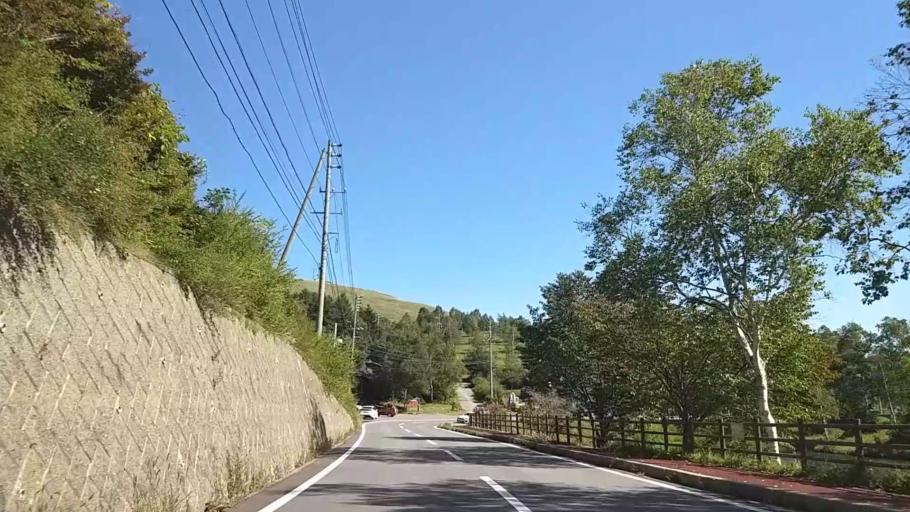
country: JP
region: Nagano
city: Chino
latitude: 36.1027
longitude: 138.2291
